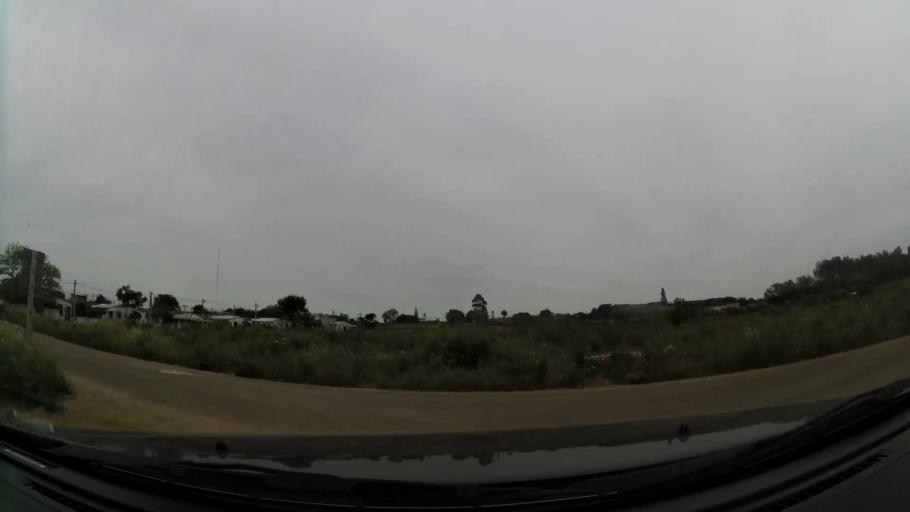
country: UY
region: Canelones
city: Las Piedras
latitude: -34.7436
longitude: -56.2197
